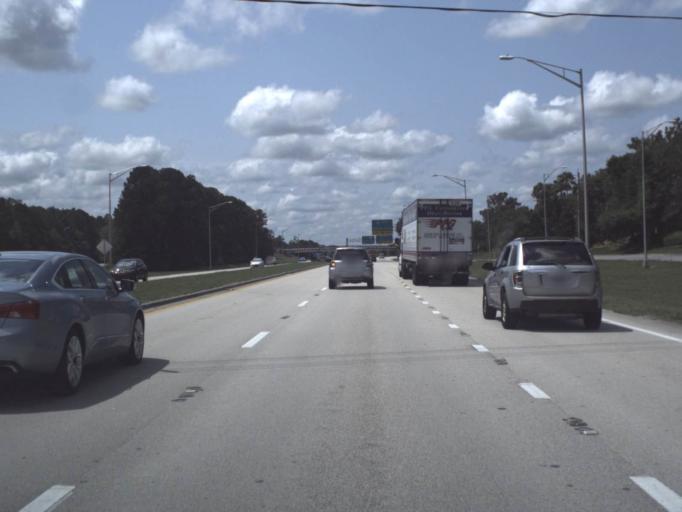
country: US
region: Florida
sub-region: Saint Johns County
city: Fruit Cove
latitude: 30.2075
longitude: -81.5519
